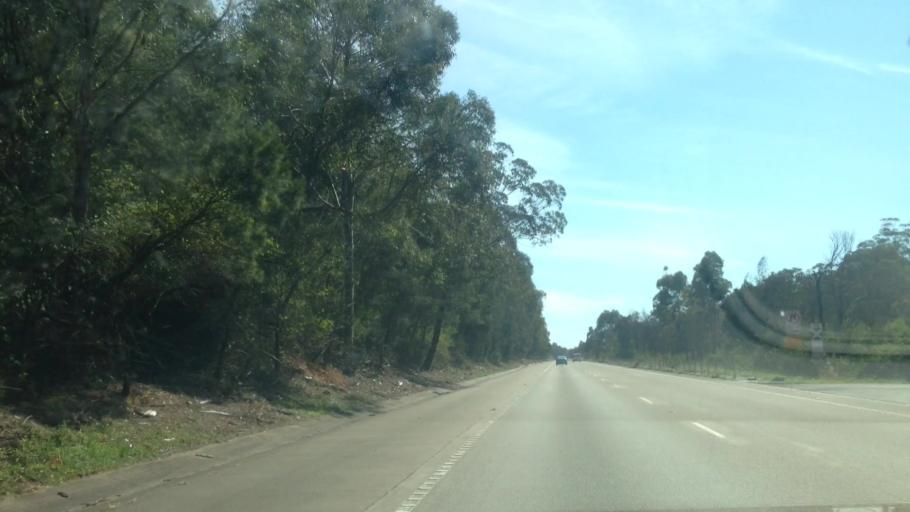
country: AU
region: New South Wales
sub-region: Lake Macquarie Shire
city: Fennell Bay
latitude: -32.9694
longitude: 151.5347
